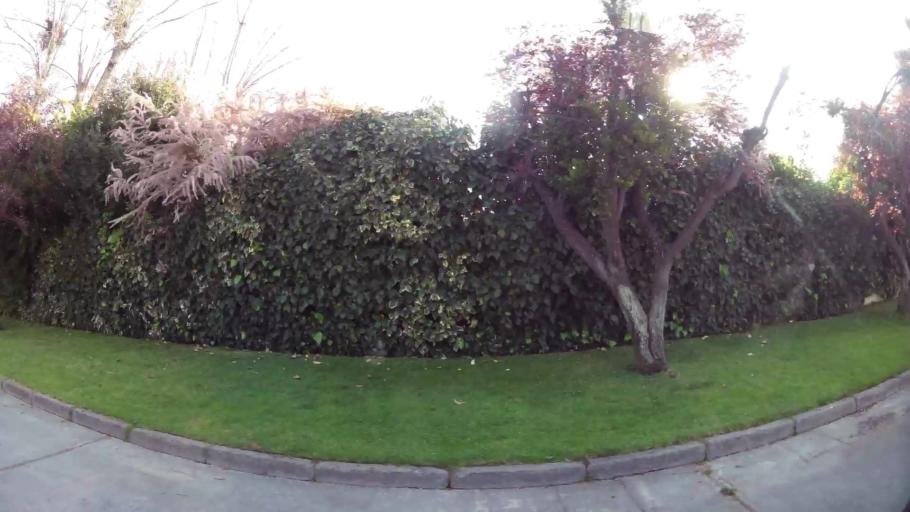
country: CL
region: Santiago Metropolitan
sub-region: Provincia de Santiago
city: Villa Presidente Frei, Nunoa, Santiago, Chile
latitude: -33.3587
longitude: -70.5288
